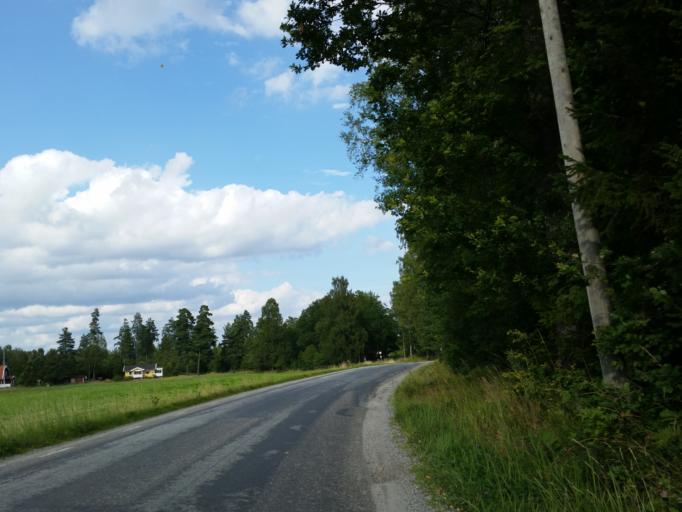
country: SE
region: Soedermanland
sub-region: Strangnas Kommun
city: Mariefred
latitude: 59.2232
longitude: 17.2987
